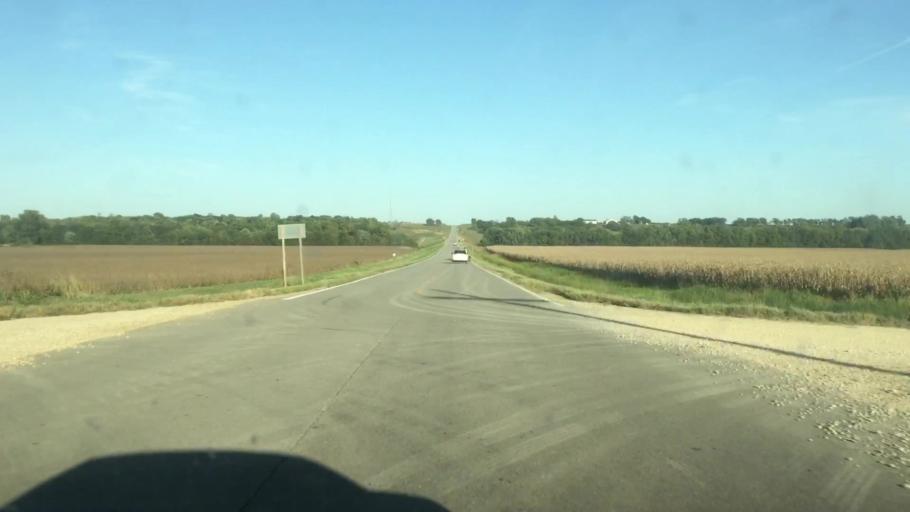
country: US
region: Kansas
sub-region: Brown County
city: Horton
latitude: 39.5875
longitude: -95.5642
